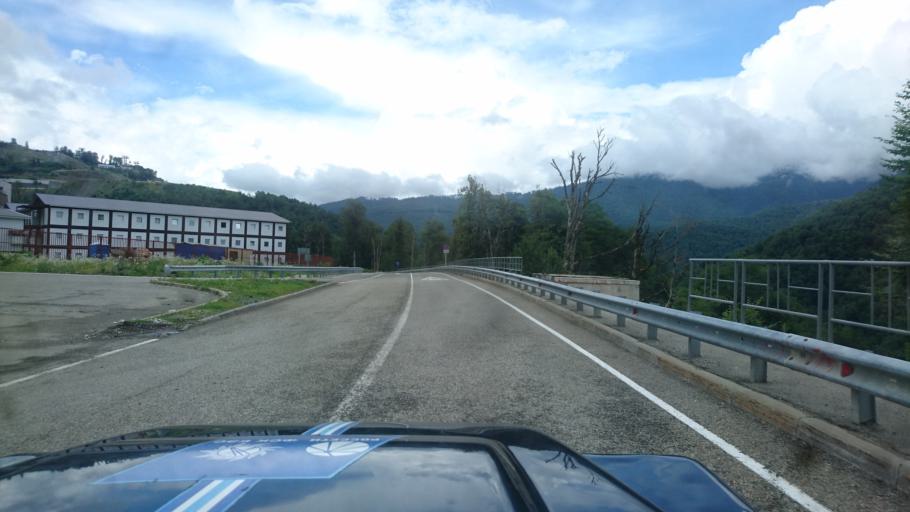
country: RU
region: Krasnodarskiy
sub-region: Sochi City
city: Krasnaya Polyana
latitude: 43.6468
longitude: 40.3403
